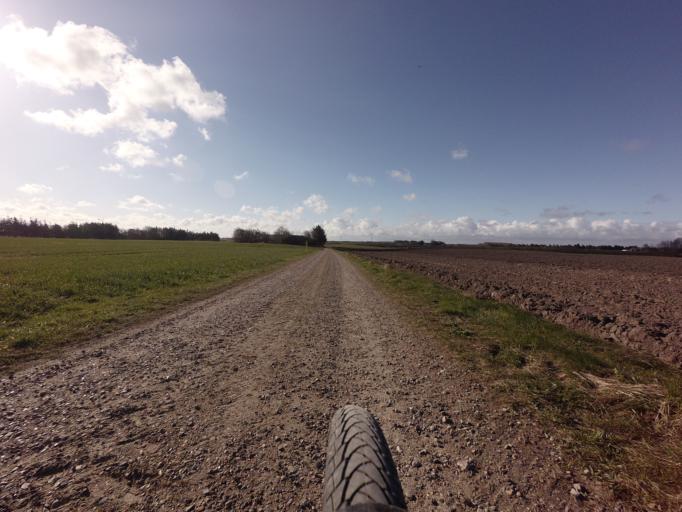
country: DK
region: North Denmark
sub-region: Hjorring Kommune
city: Vra
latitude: 57.3624
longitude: 9.8167
